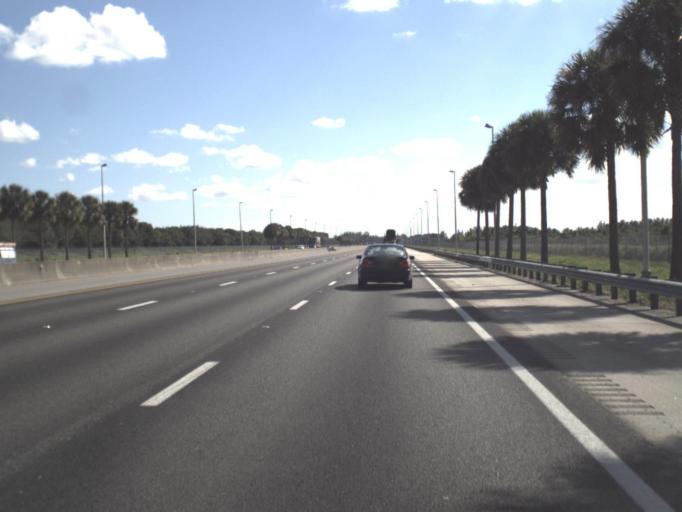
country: US
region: Florida
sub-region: Palm Beach County
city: Villages of Oriole
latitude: 26.4986
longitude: -80.1727
